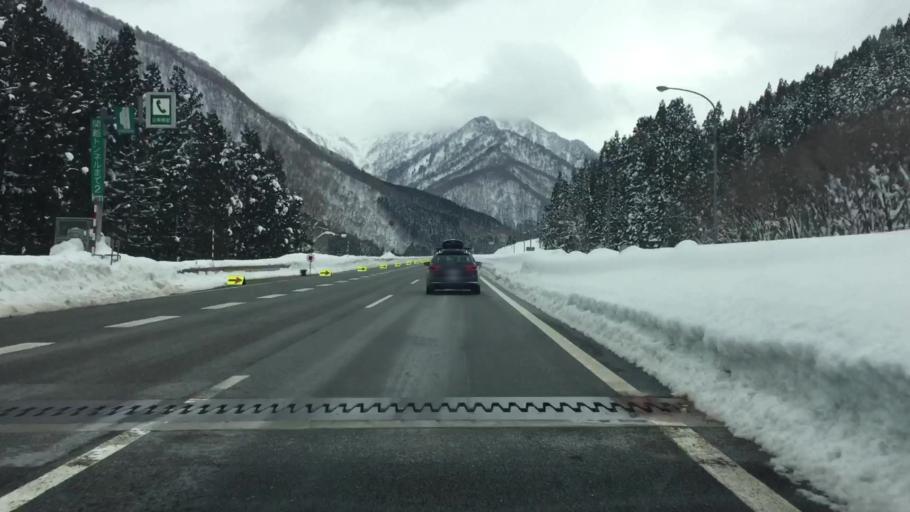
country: JP
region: Niigata
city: Shiozawa
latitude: 36.8795
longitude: 138.8564
